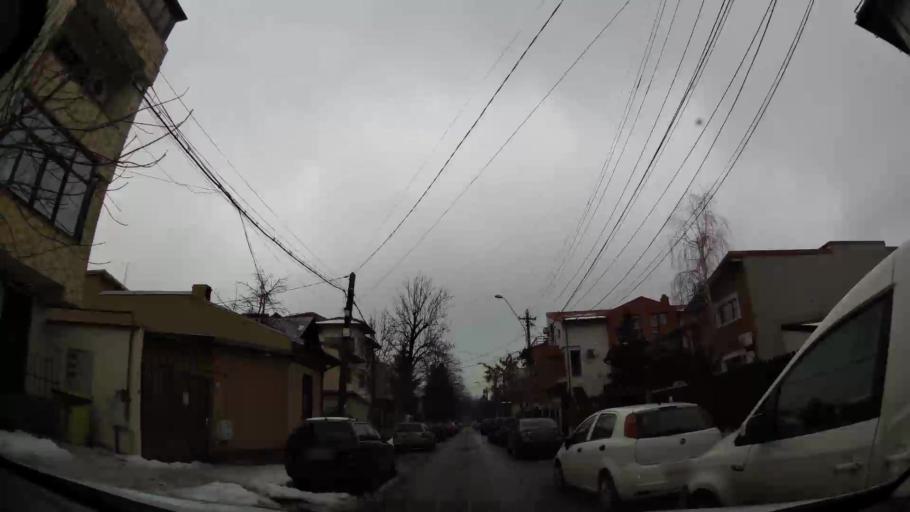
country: RO
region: Bucuresti
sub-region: Municipiul Bucuresti
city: Bucuresti
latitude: 44.4625
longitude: 26.0702
